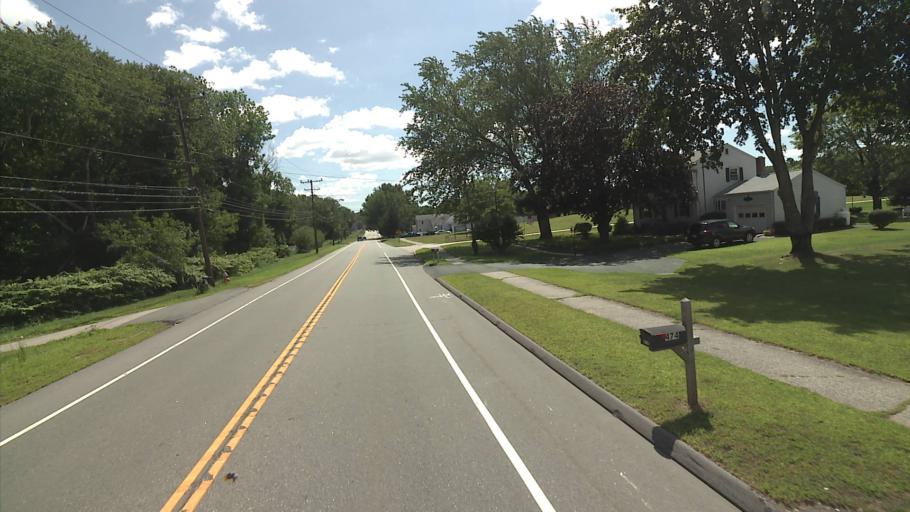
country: US
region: Connecticut
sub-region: New London County
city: Niantic
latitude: 41.3613
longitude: -72.1781
